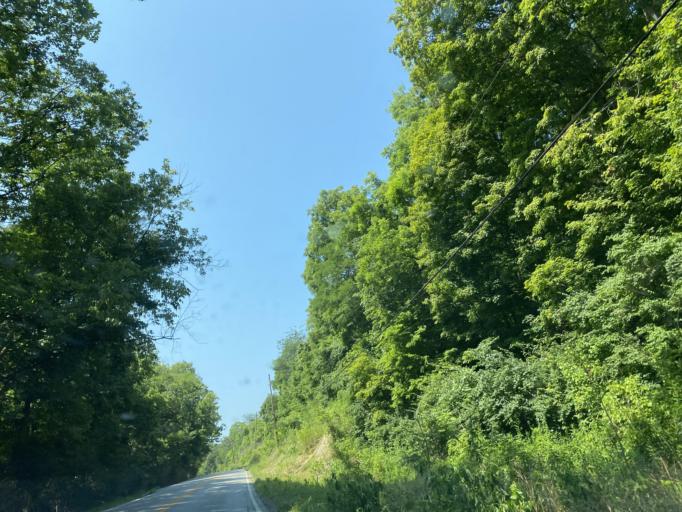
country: US
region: Kentucky
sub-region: Campbell County
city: Claryville
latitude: 38.8942
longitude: -84.4460
